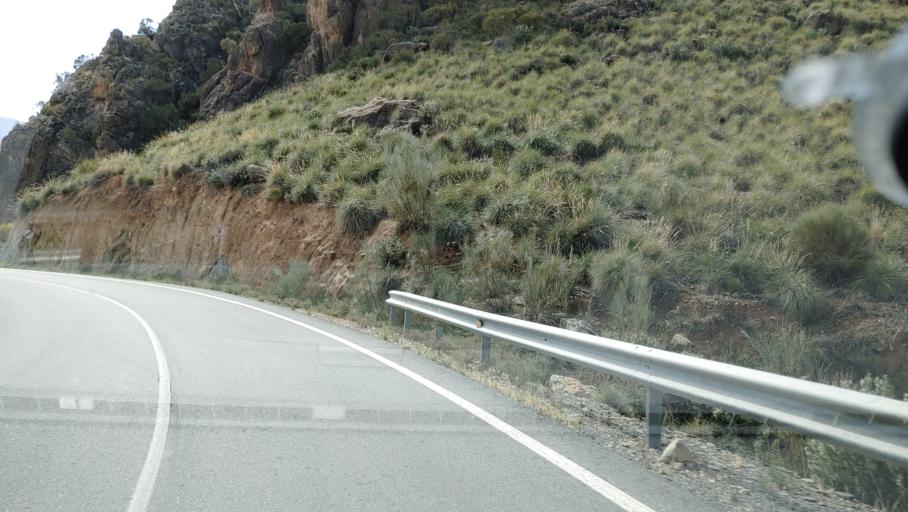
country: ES
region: Andalusia
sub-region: Provincia de Almeria
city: Canjayar
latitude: 37.0249
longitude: -2.7271
